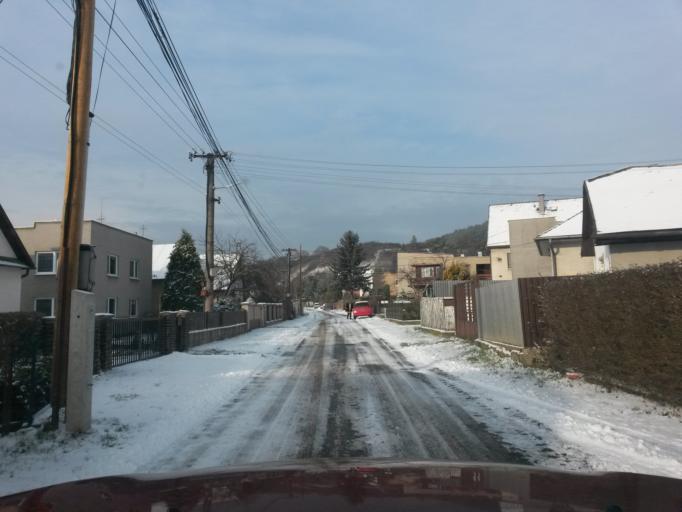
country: SK
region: Kosicky
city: Kosice
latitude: 48.8055
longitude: 21.2449
